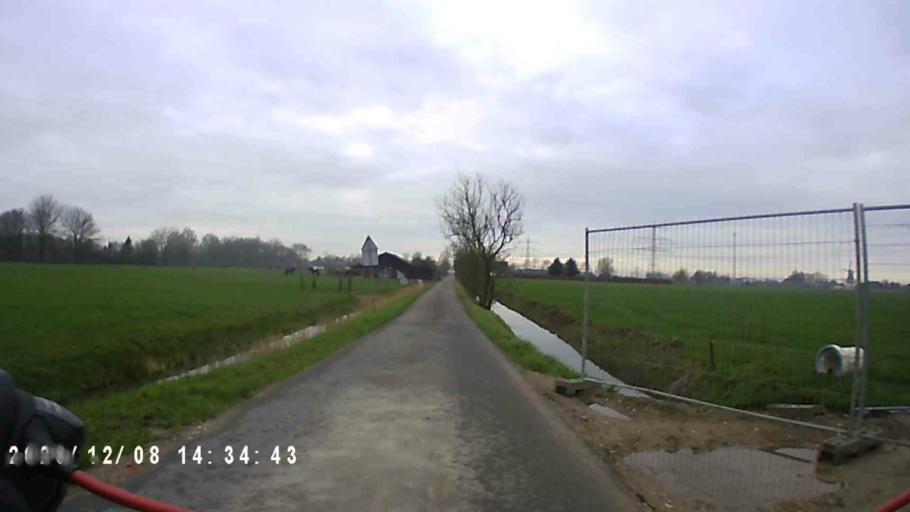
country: NL
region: Groningen
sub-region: Gemeente Winsum
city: Winsum
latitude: 53.2979
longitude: 6.5405
